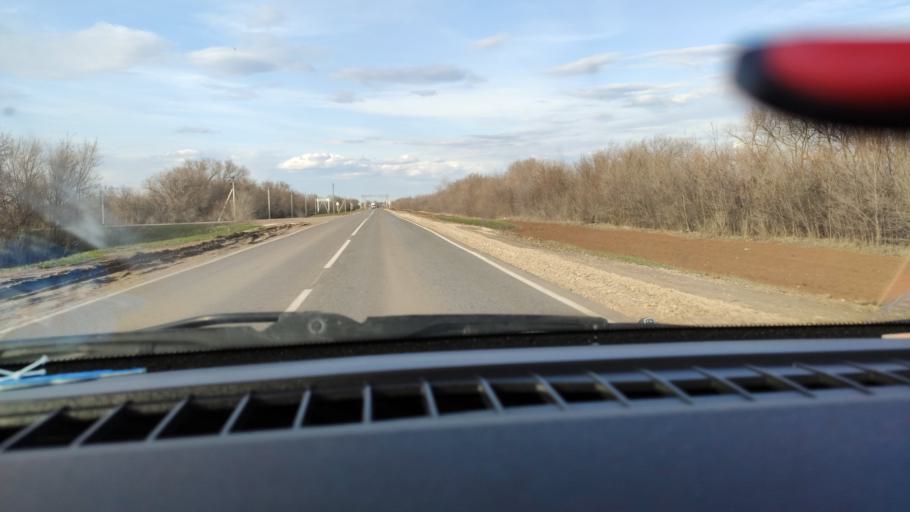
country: RU
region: Saratov
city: Privolzhskiy
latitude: 51.3237
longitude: 46.0286
